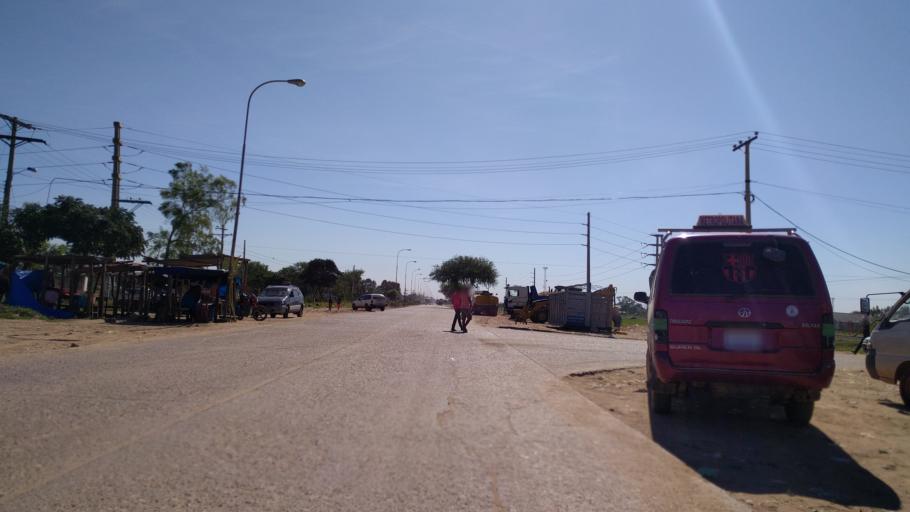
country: BO
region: Santa Cruz
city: Santa Cruz de la Sierra
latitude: -17.8736
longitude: -63.1930
